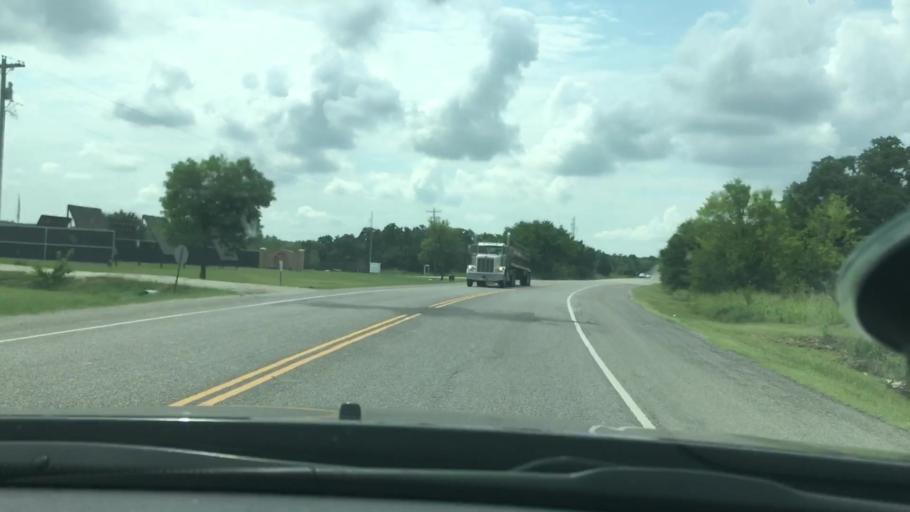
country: US
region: Oklahoma
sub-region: Carter County
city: Ardmore
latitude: 34.1995
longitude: -97.1083
